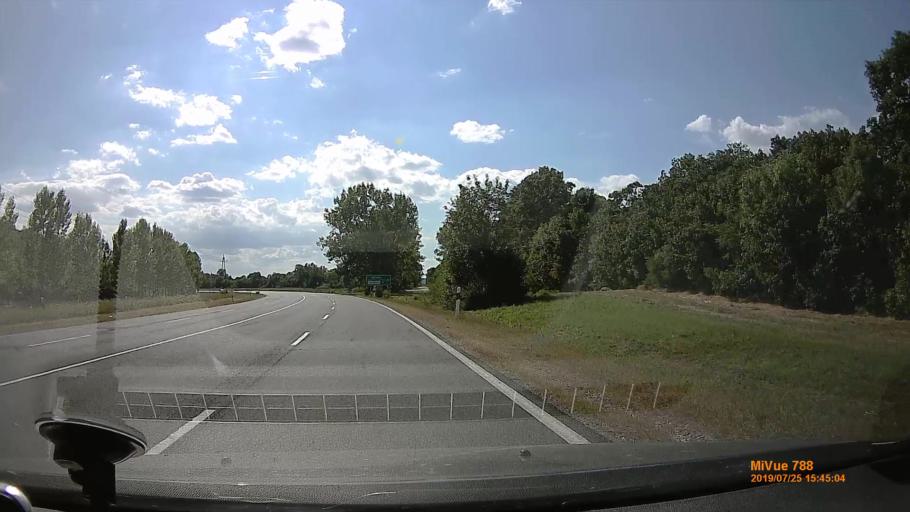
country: HU
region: Borsod-Abauj-Zemplen
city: Harsany
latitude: 47.9215
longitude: 20.7270
